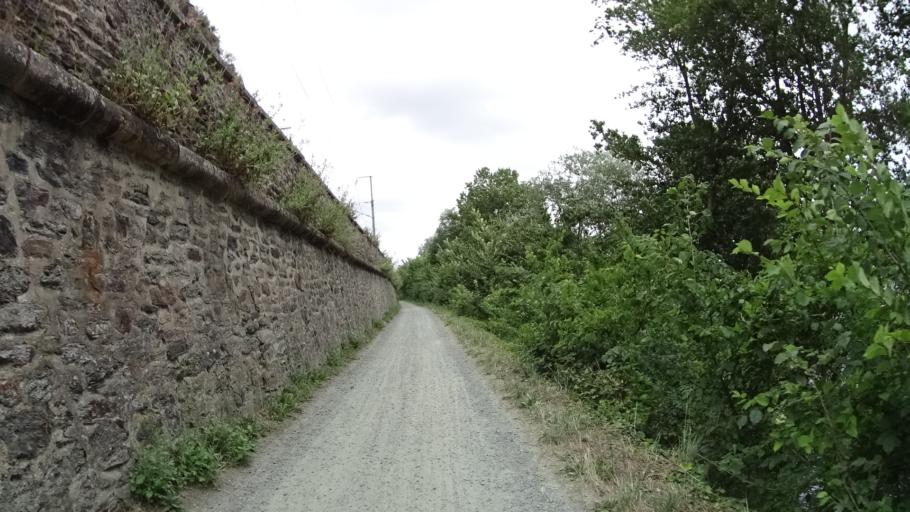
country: FR
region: Pays de la Loire
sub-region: Departement de la Loire-Atlantique
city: Mauves-sur-Loire
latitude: 47.2976
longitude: -1.3755
